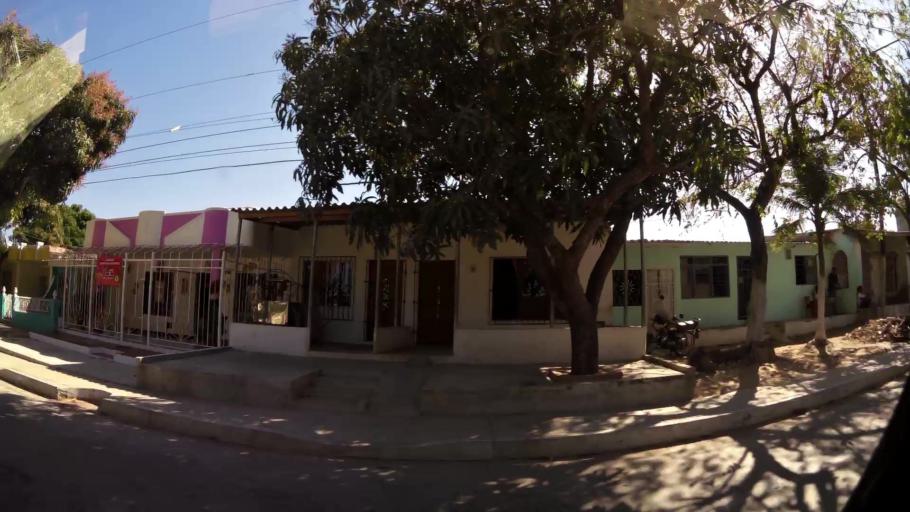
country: CO
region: Atlantico
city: Barranquilla
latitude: 10.9314
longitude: -74.8120
